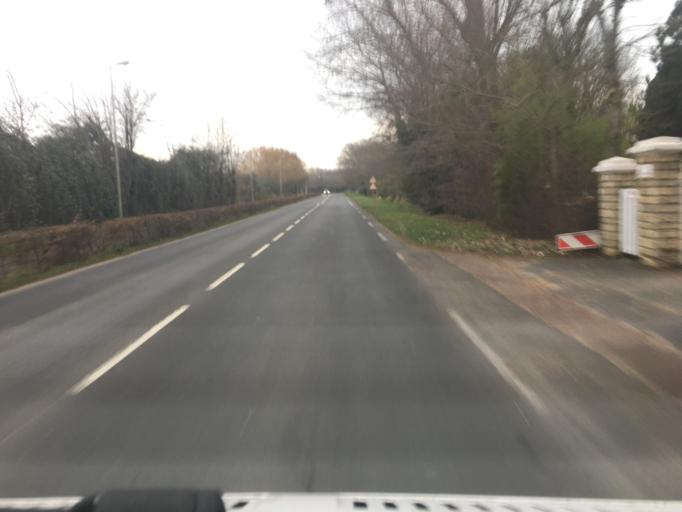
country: FR
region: Lower Normandy
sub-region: Departement du Calvados
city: Merville-Franceville-Plage
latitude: 49.2847
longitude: -0.1805
